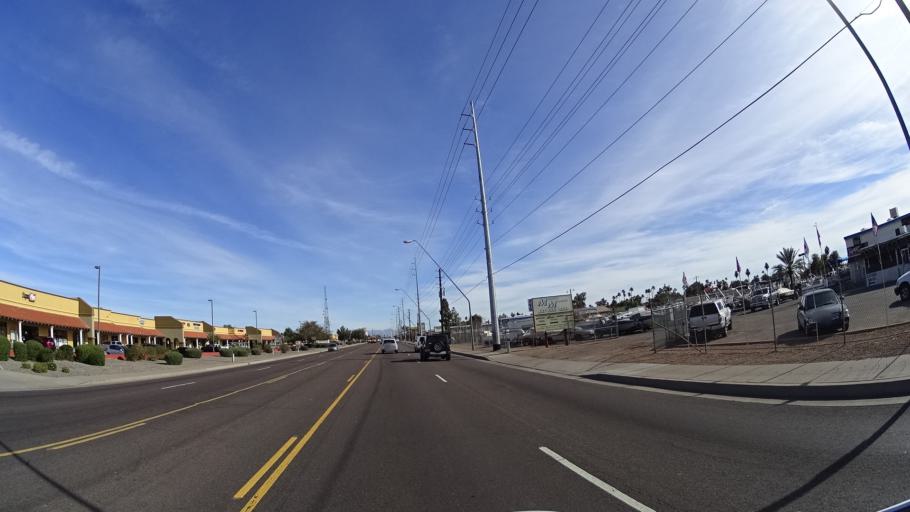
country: US
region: Arizona
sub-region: Maricopa County
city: Mesa
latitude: 33.4077
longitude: -111.8471
